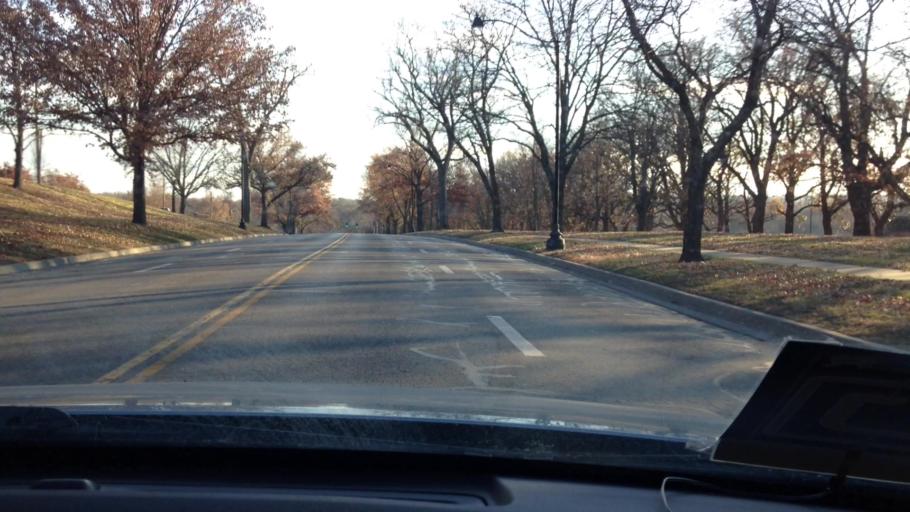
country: US
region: Kansas
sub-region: Leavenworth County
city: Leavenworth
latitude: 39.3409
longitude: -94.9213
